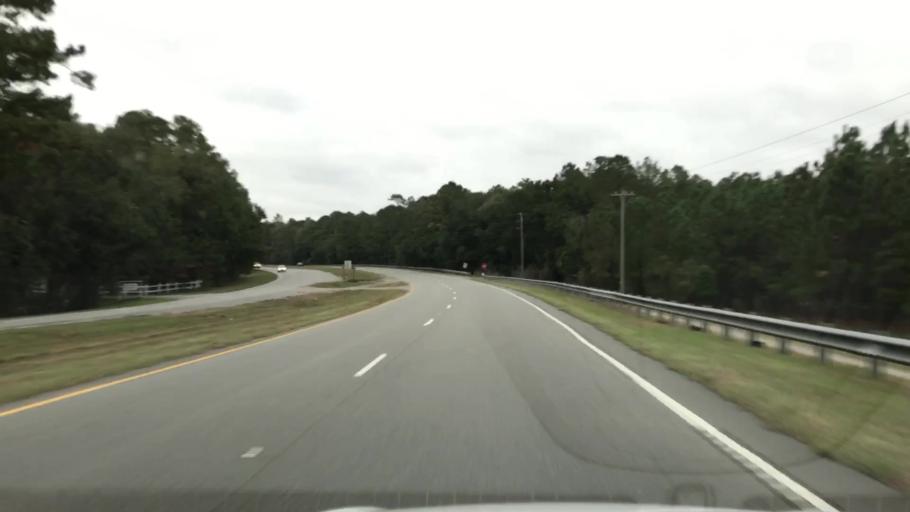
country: US
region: South Carolina
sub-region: Georgetown County
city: Georgetown
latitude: 33.2114
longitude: -79.3821
